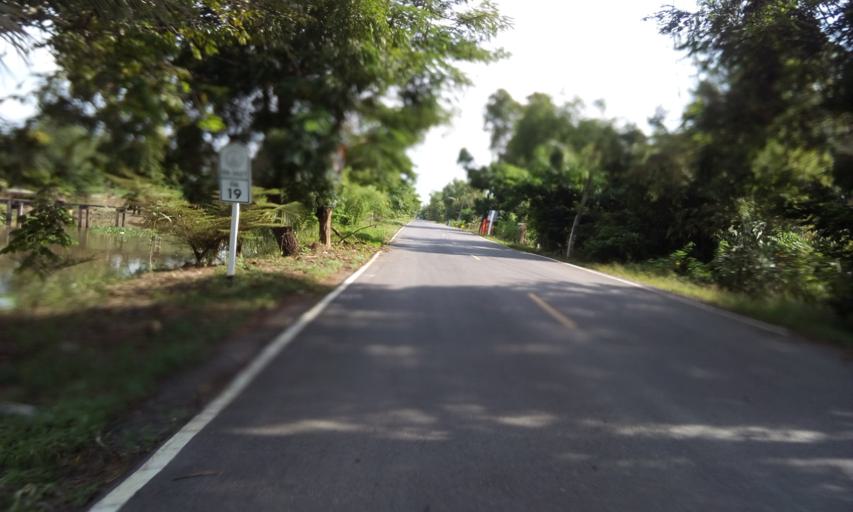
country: TH
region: Pathum Thani
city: Nong Suea
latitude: 14.2245
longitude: 100.8229
